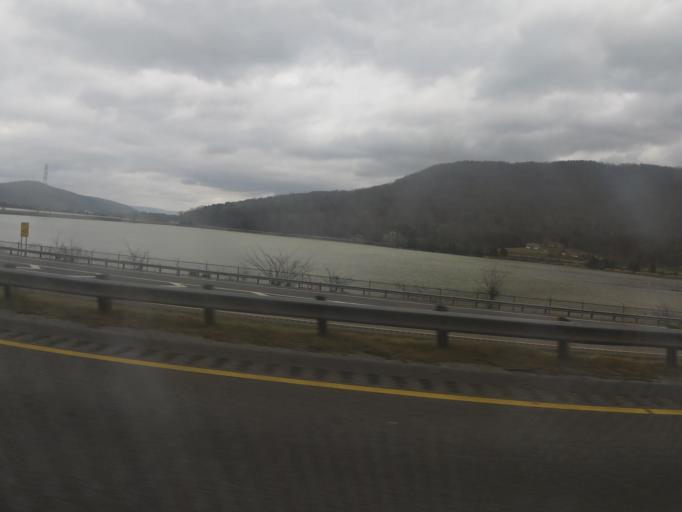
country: US
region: Tennessee
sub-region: Marion County
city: Jasper
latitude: 35.0136
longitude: -85.5375
